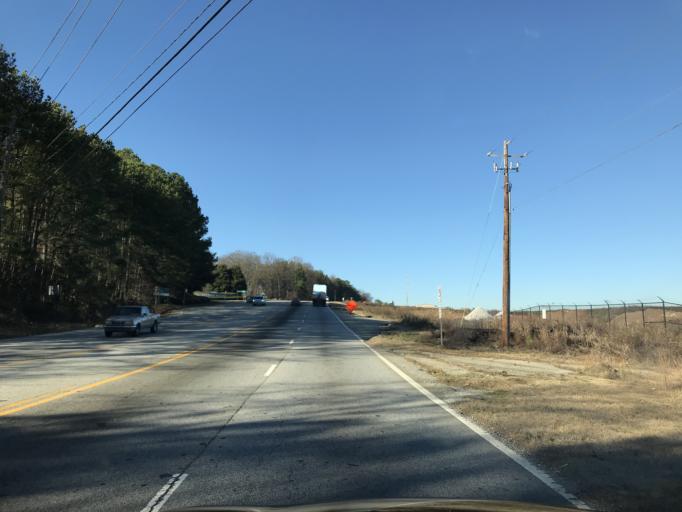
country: US
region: Georgia
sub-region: Fulton County
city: Hapeville
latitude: 33.6178
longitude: -84.4115
